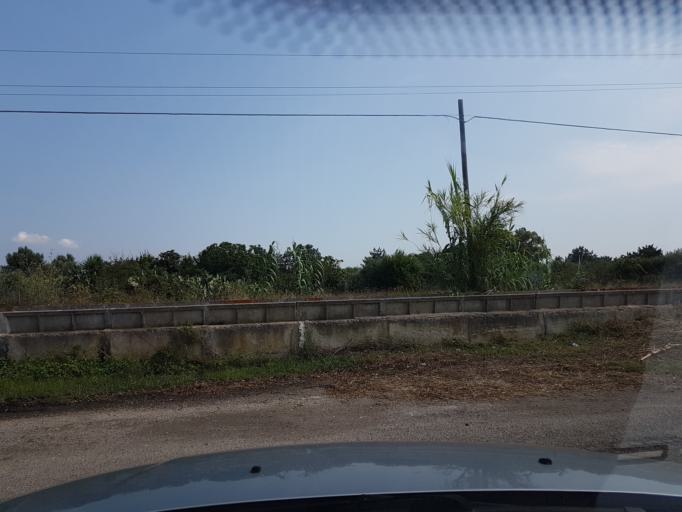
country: IT
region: Sardinia
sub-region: Provincia di Oristano
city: Donigala Fenugheddu
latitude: 39.9365
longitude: 8.5781
